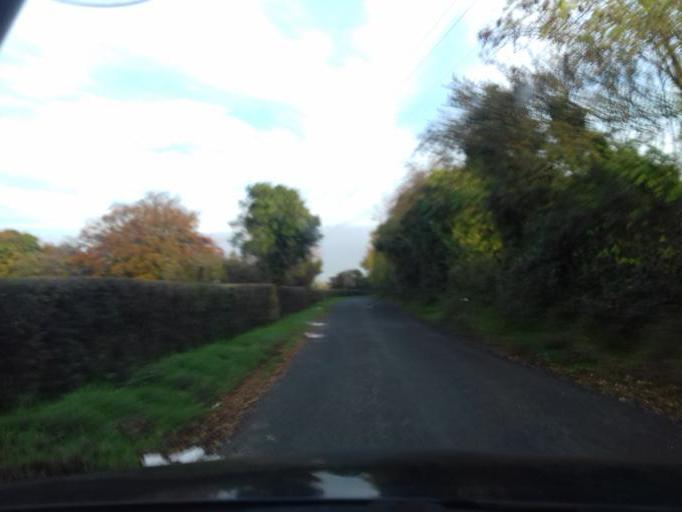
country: IE
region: Leinster
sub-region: An Mhi
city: Dunboyne
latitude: 53.3870
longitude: -6.4647
